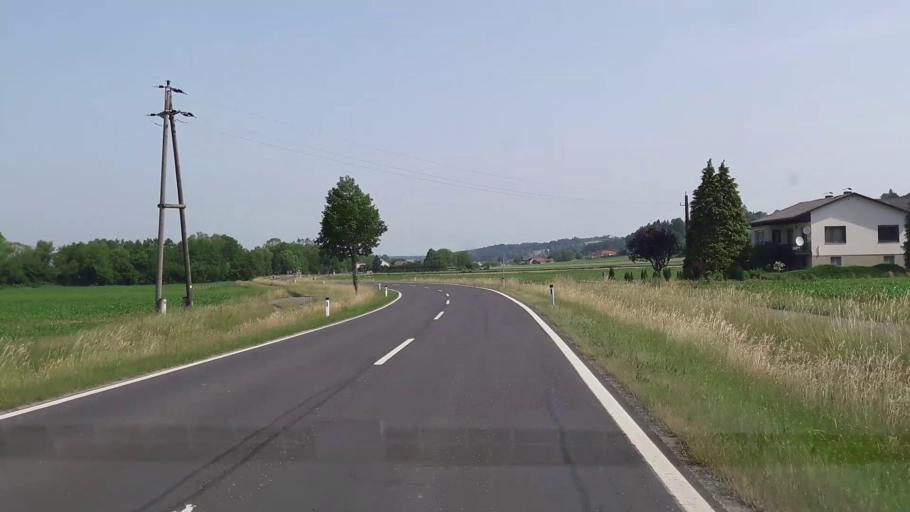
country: AT
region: Styria
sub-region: Politischer Bezirk Hartberg-Fuerstenfeld
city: Burgau
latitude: 47.1288
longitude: 16.1158
